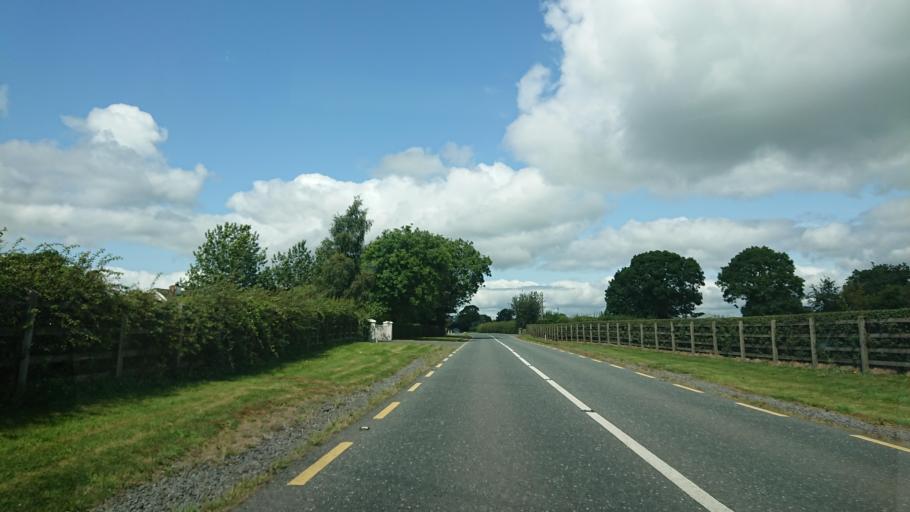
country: IE
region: Leinster
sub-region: Kildare
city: Kilcock
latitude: 53.3789
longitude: -6.7035
